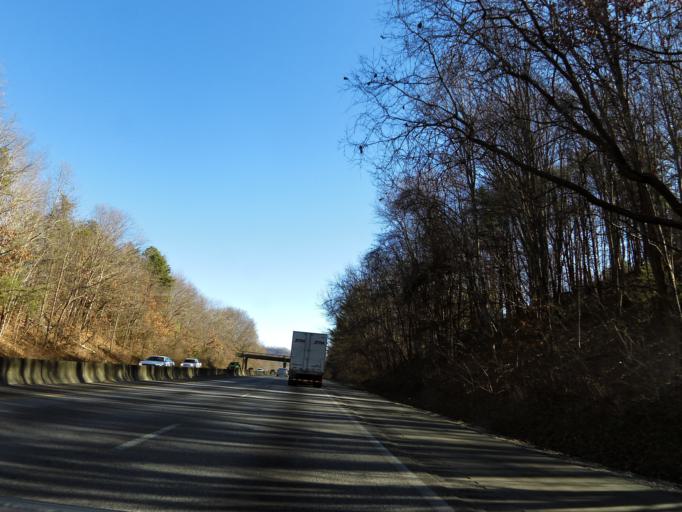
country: US
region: North Carolina
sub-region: Haywood County
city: West Canton
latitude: 35.5544
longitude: -82.8604
